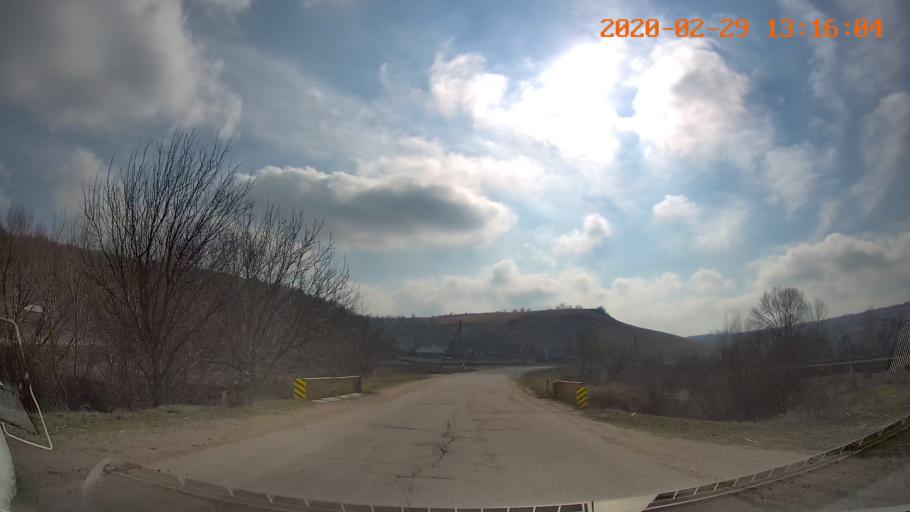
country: MD
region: Telenesti
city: Camenca
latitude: 48.0054
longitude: 28.6666
